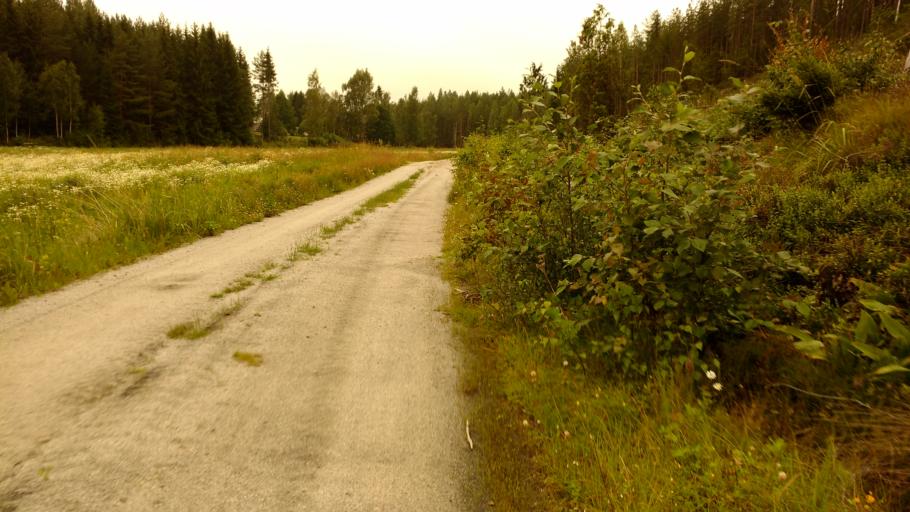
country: FI
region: Varsinais-Suomi
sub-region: Salo
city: Pertteli
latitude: 60.4053
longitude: 23.2273
